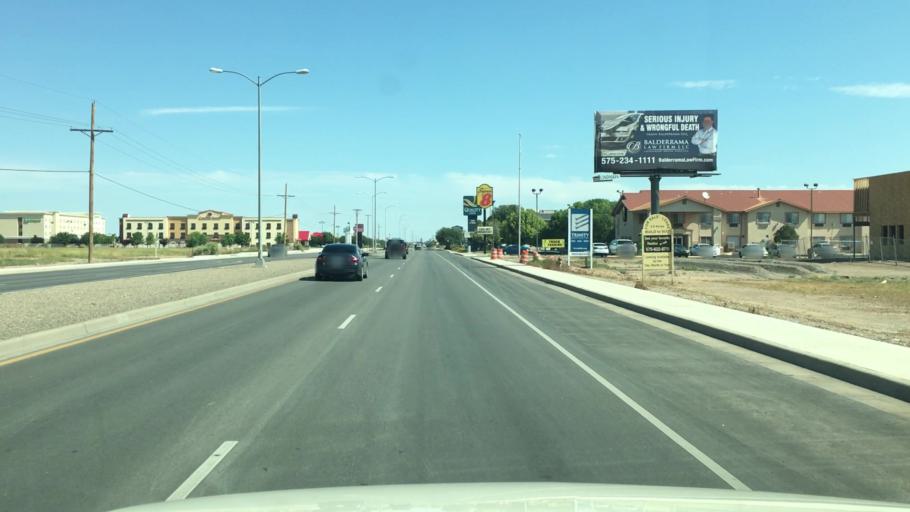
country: US
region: New Mexico
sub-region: Chaves County
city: Roswell
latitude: 33.4392
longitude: -104.5231
